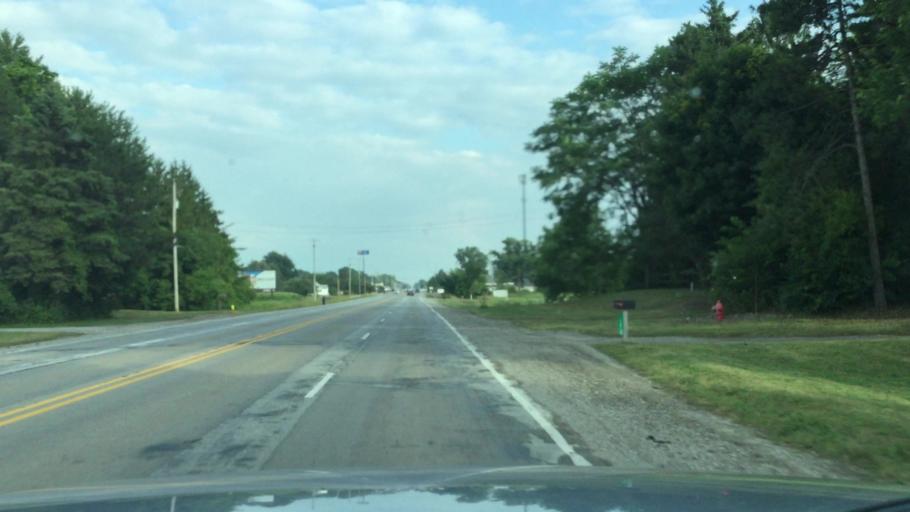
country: US
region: Michigan
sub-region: Saginaw County
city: Birch Run
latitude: 43.2567
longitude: -83.7743
